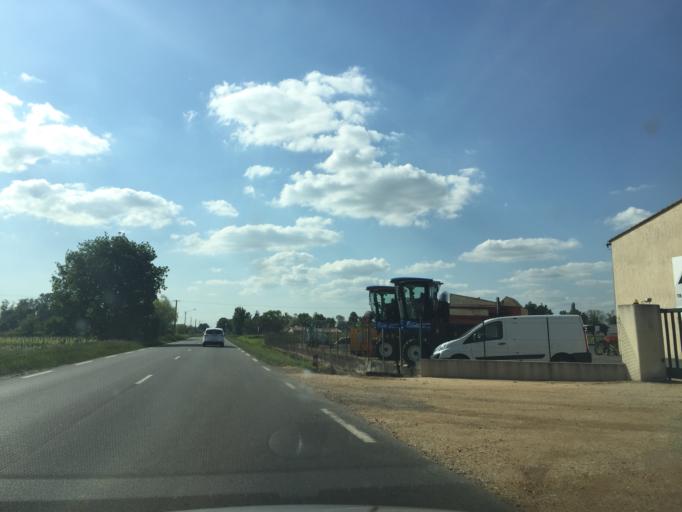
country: FR
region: Aquitaine
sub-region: Departement de la Gironde
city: Saint-Sulpice-de-Faleyrens
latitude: 44.8890
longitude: -0.1886
